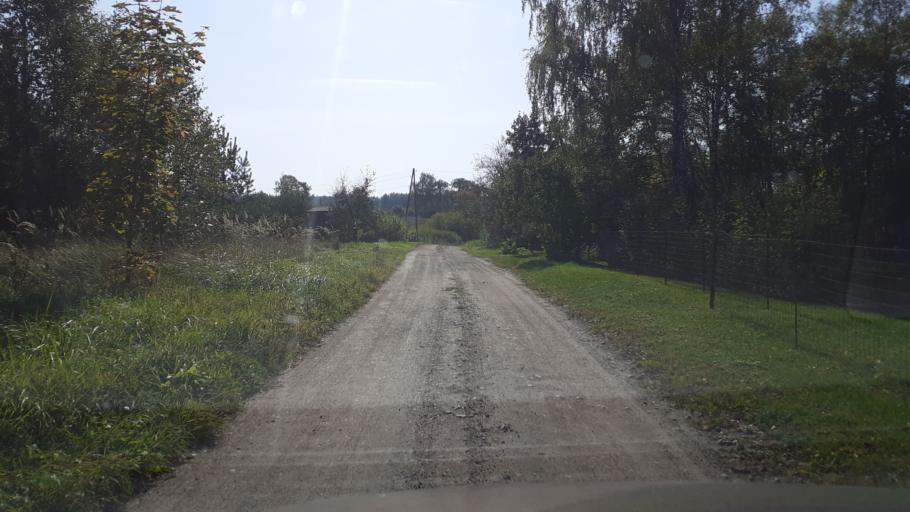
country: LV
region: Kuldigas Rajons
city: Kuldiga
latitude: 56.9483
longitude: 21.9942
